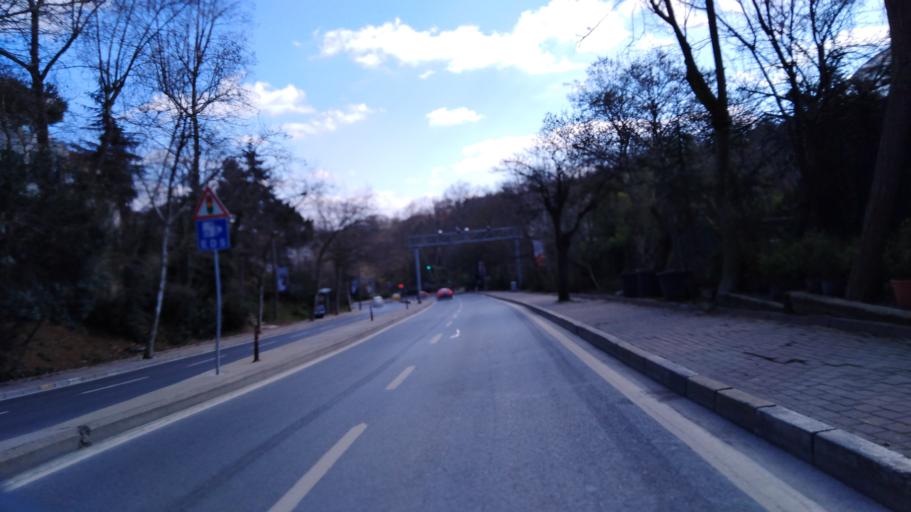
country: TR
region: Istanbul
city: Sisli
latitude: 41.1109
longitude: 29.0472
